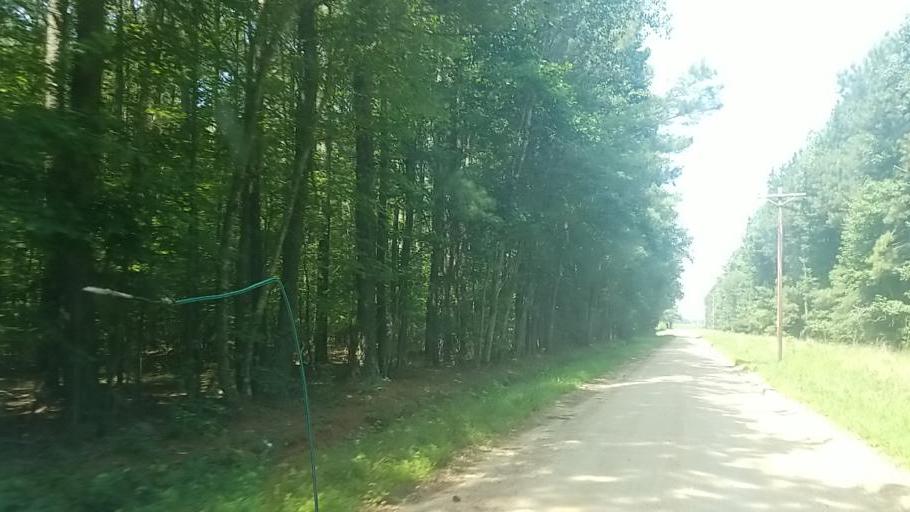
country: US
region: Maryland
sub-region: Caroline County
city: Denton
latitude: 38.8706
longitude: -75.7444
